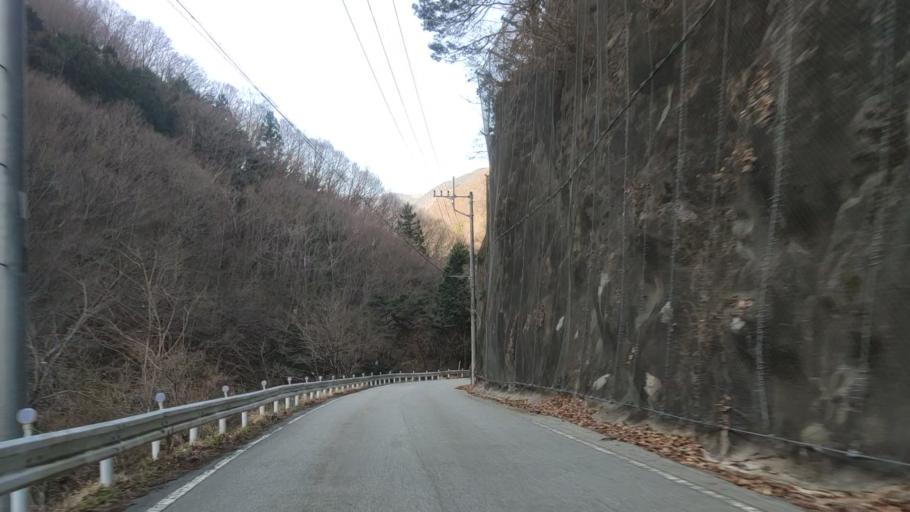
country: JP
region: Yamanashi
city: Fujikawaguchiko
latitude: 35.5375
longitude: 138.6267
